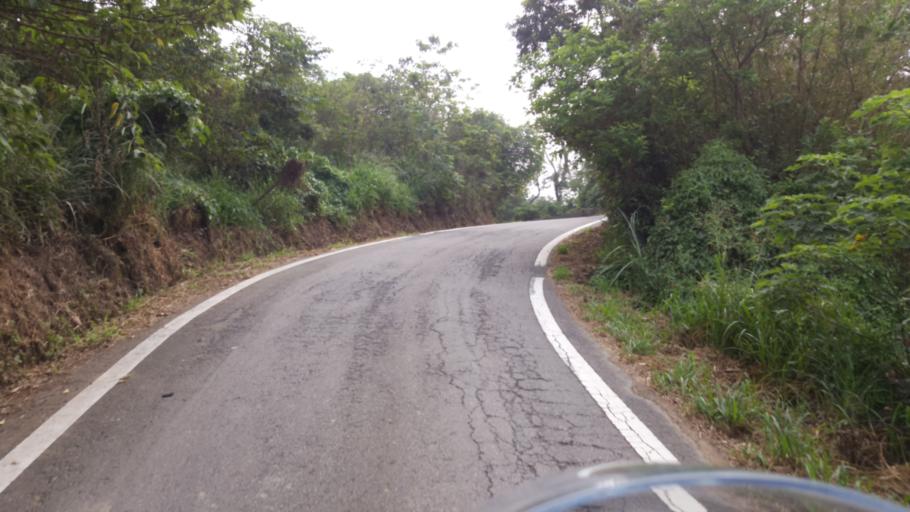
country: TW
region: Taiwan
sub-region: Hsinchu
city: Hsinchu
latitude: 24.7491
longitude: 120.9552
